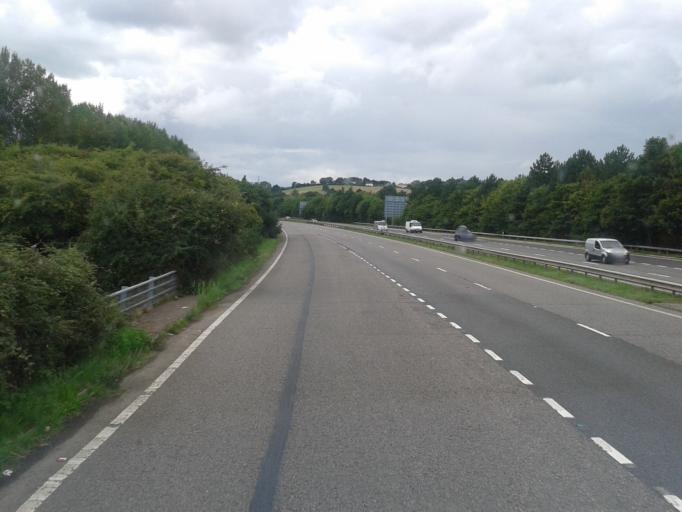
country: GB
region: England
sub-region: Devon
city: Exeter
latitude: 50.7032
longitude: -3.5478
